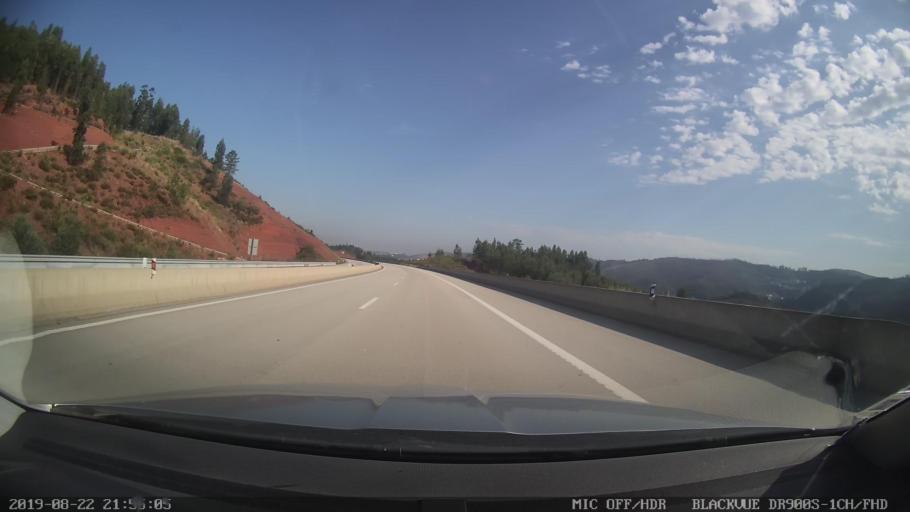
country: PT
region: Coimbra
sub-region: Coimbra
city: Coimbra
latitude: 40.1472
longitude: -8.3830
